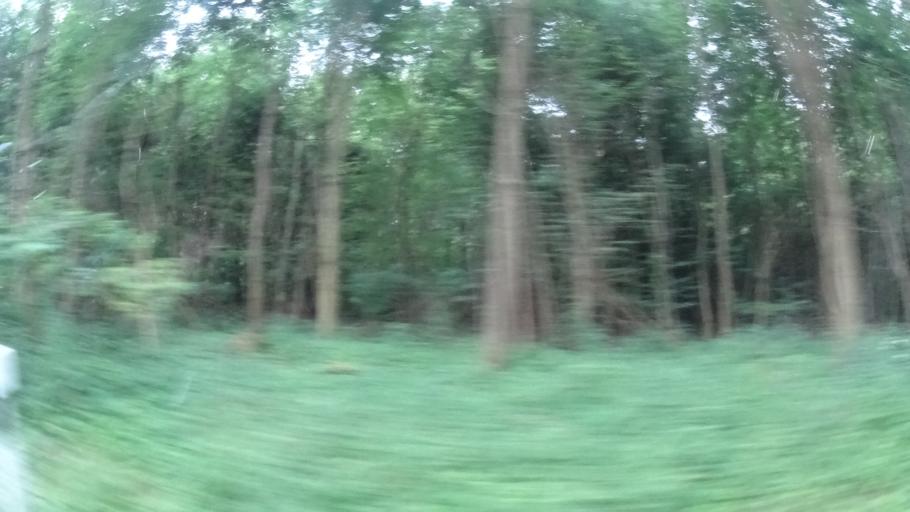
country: DE
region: Lower Saxony
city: Heinsen
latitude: 51.8954
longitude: 9.4630
